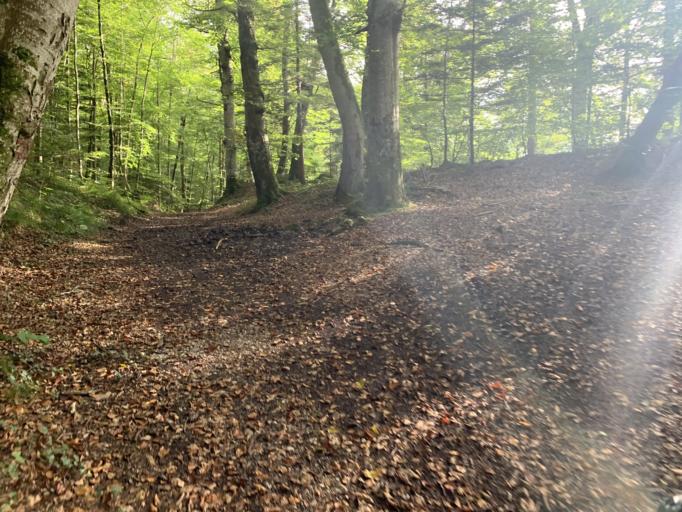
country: DE
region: Bavaria
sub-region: Upper Bavaria
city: Baierbrunn
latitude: 48.0233
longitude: 11.4978
